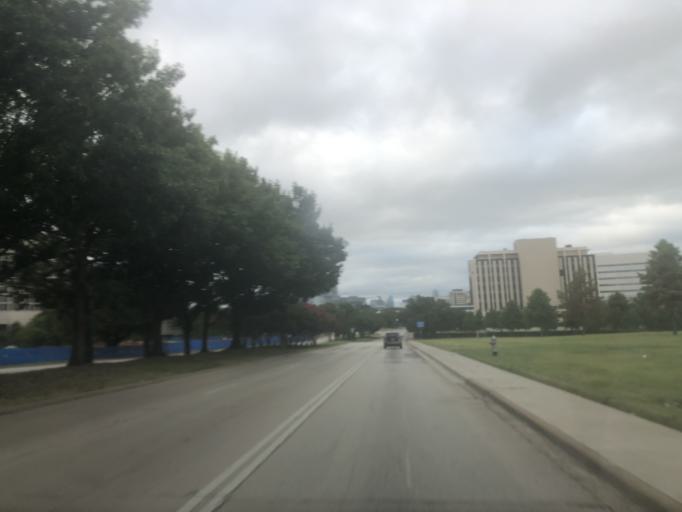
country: US
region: Texas
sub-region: Dallas County
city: Dallas
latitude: 32.8200
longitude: -96.8475
